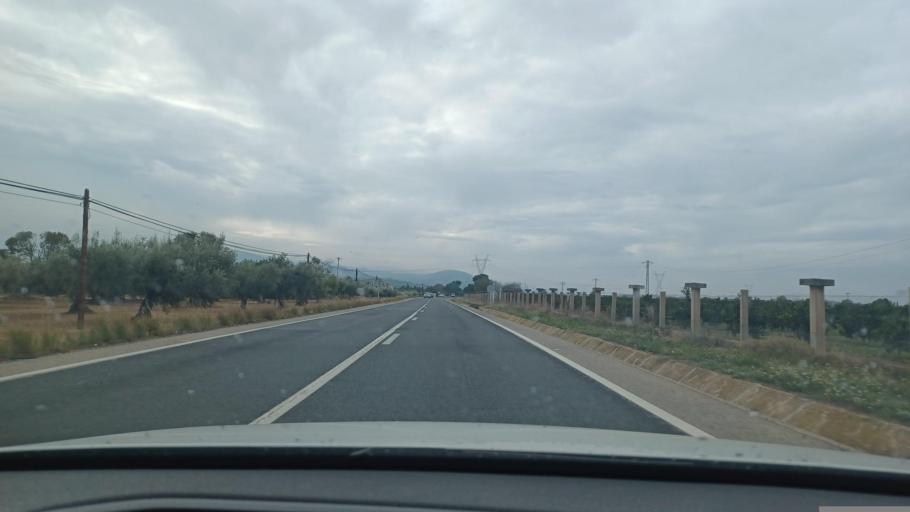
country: ES
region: Catalonia
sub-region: Provincia de Tarragona
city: Santa Barbara
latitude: 40.6971
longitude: 0.4768
